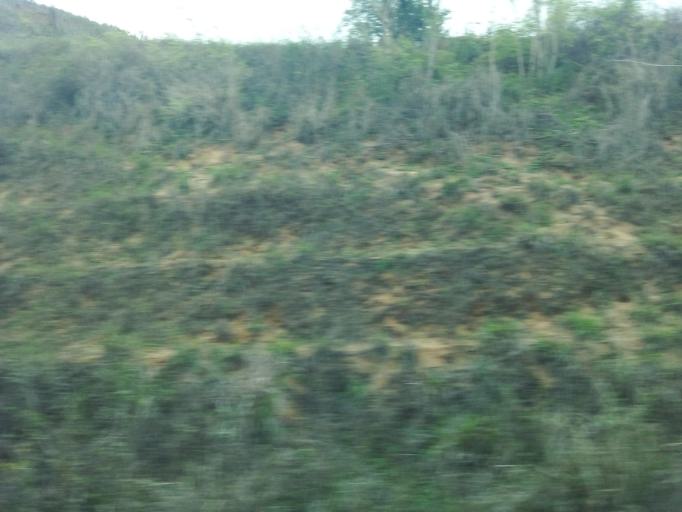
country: BR
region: Minas Gerais
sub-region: Belo Oriente
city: Belo Oriente
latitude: -19.2252
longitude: -42.3002
